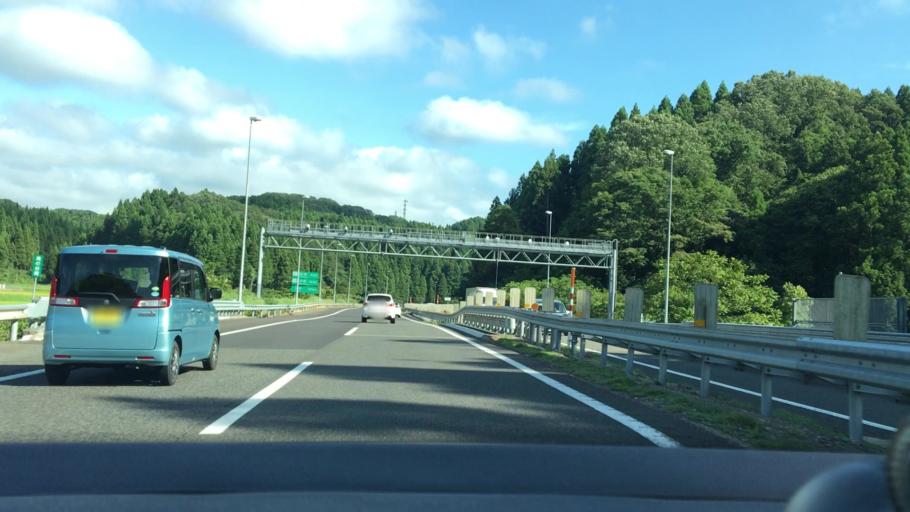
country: JP
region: Fukui
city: Maruoka
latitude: 36.2818
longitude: 136.2784
